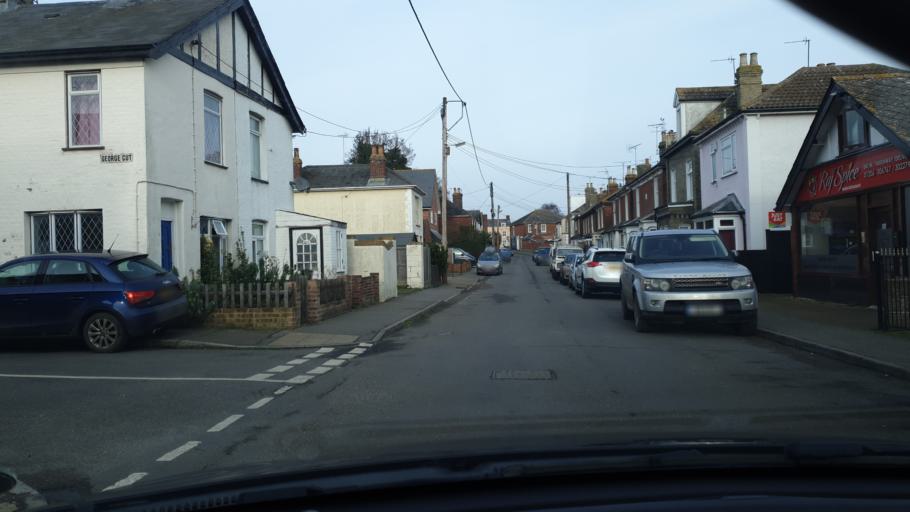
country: GB
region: England
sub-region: Essex
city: Brightlingsea
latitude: 51.8091
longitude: 1.0268
